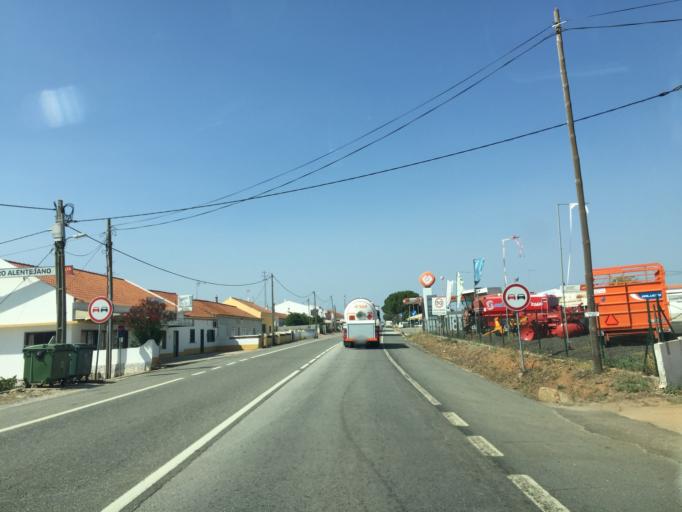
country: PT
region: Beja
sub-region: Aljustrel
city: Aljustrel
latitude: 37.9452
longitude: -8.3805
